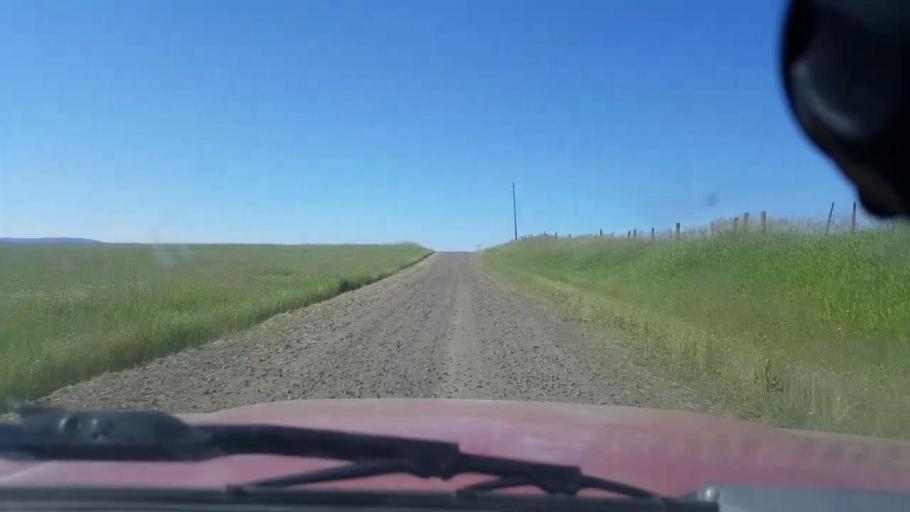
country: US
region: Washington
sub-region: Garfield County
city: Pomeroy
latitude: 45.9881
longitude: -117.4580
